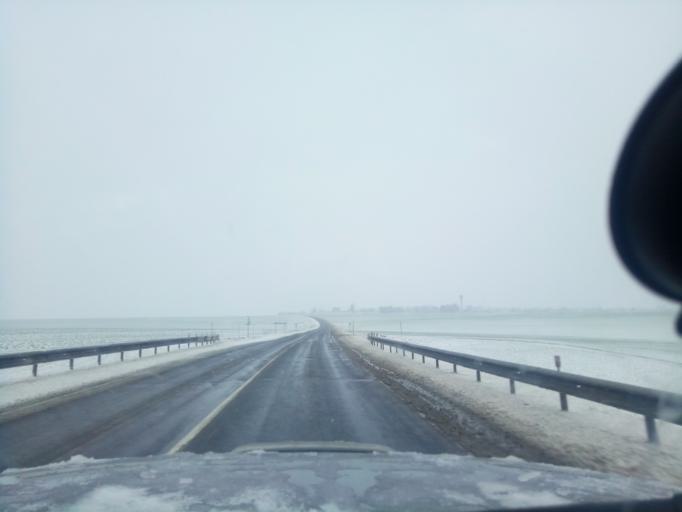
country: BY
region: Minsk
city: Haradzyeya
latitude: 53.3274
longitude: 26.5512
